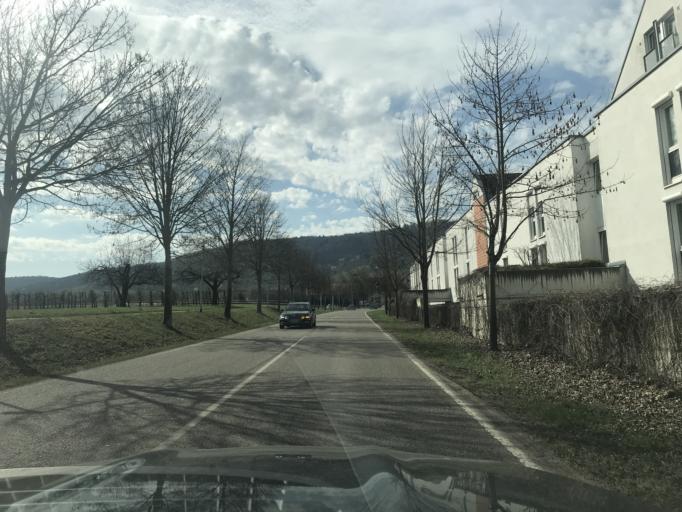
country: DE
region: Baden-Wuerttemberg
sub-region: Regierungsbezirk Stuttgart
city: Fellbach
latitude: 48.8075
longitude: 9.2877
